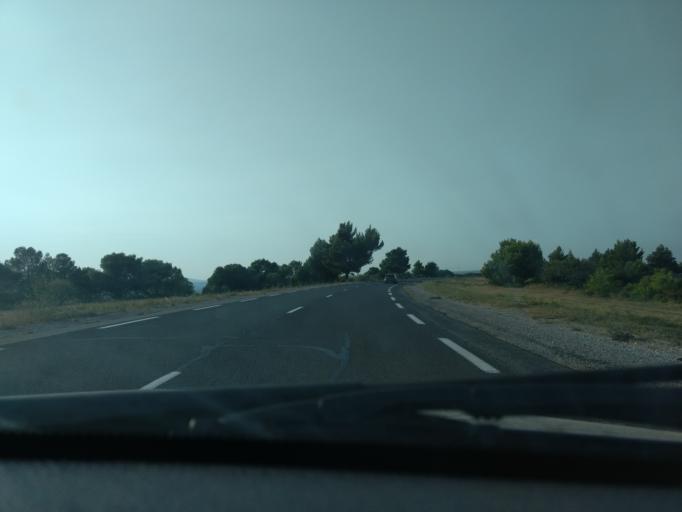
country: FR
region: Languedoc-Roussillon
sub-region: Departement de l'Aude
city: Leucate
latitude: 42.9203
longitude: 3.0180
